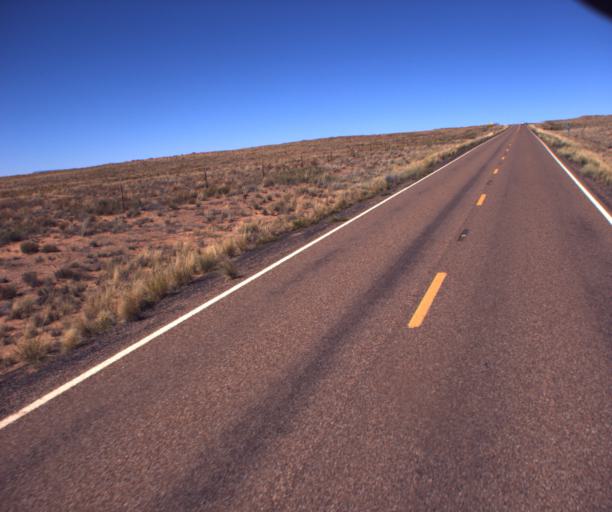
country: US
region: Arizona
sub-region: Navajo County
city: Holbrook
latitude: 34.9985
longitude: -110.0893
